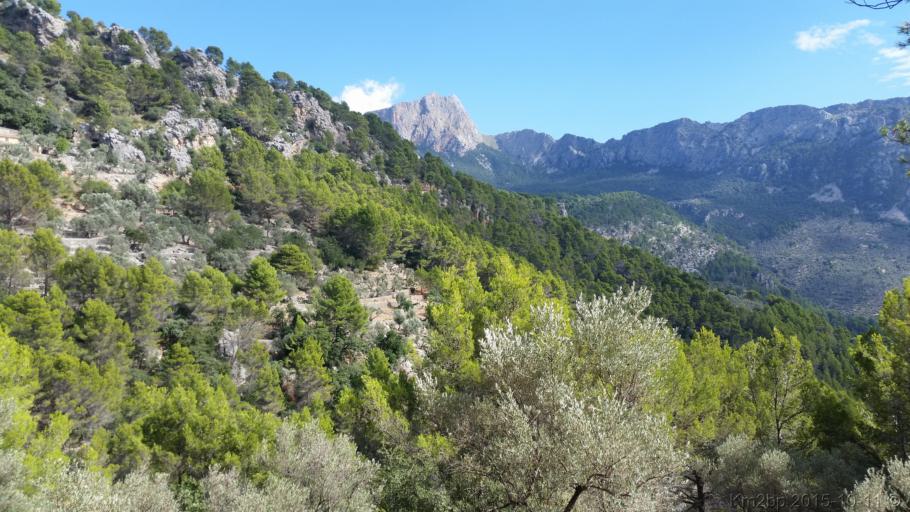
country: ES
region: Balearic Islands
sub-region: Illes Balears
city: Fornalutx
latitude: 39.7904
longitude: 2.7328
